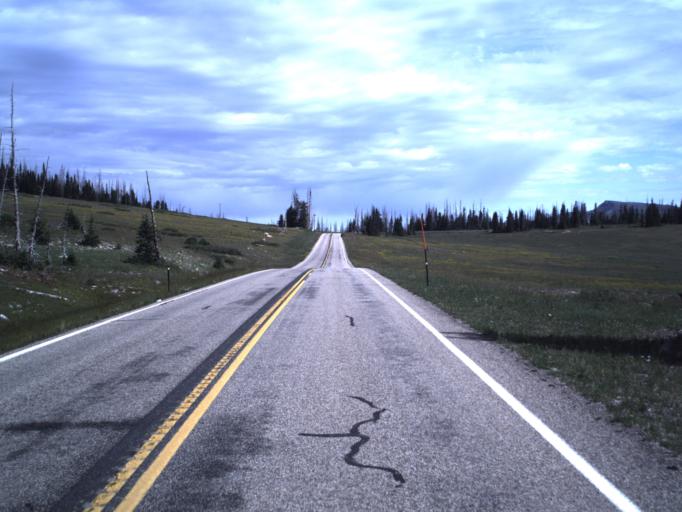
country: US
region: Utah
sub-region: Iron County
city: Cedar City
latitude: 37.6001
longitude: -112.8503
